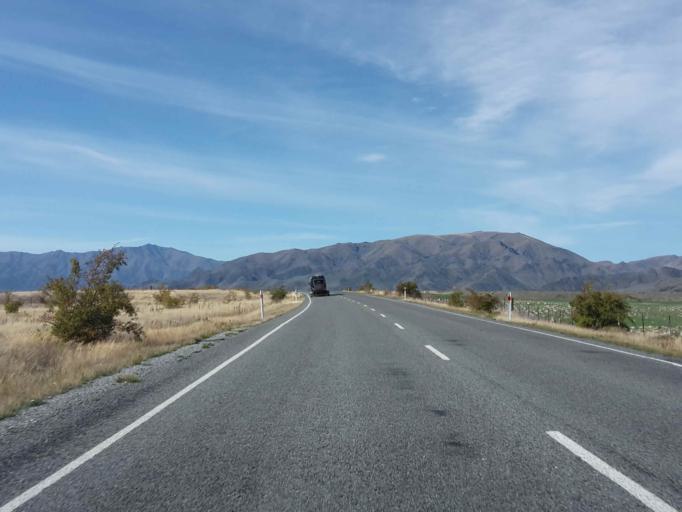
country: NZ
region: Otago
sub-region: Queenstown-Lakes District
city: Wanaka
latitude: -44.5146
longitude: 169.8251
